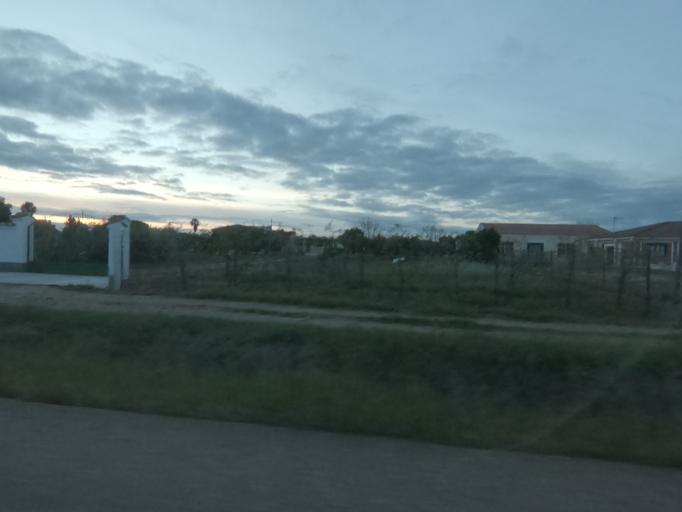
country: ES
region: Extremadura
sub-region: Provincia de Badajoz
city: Badajoz
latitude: 38.9274
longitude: -6.9344
